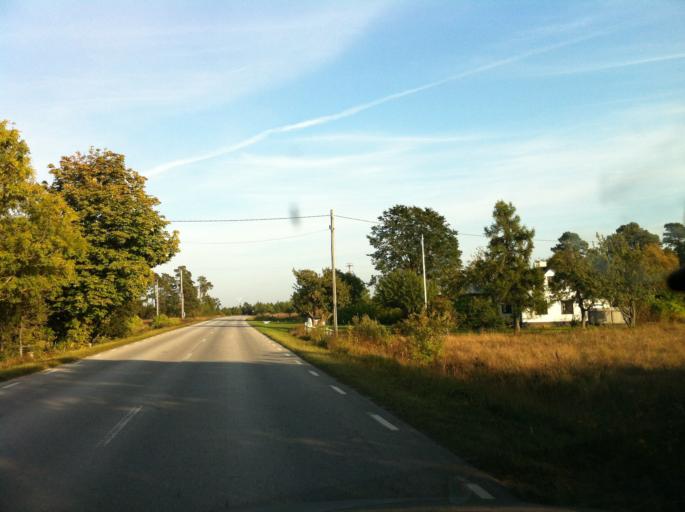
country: SE
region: Gotland
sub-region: Gotland
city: Slite
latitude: 57.4411
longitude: 18.7364
